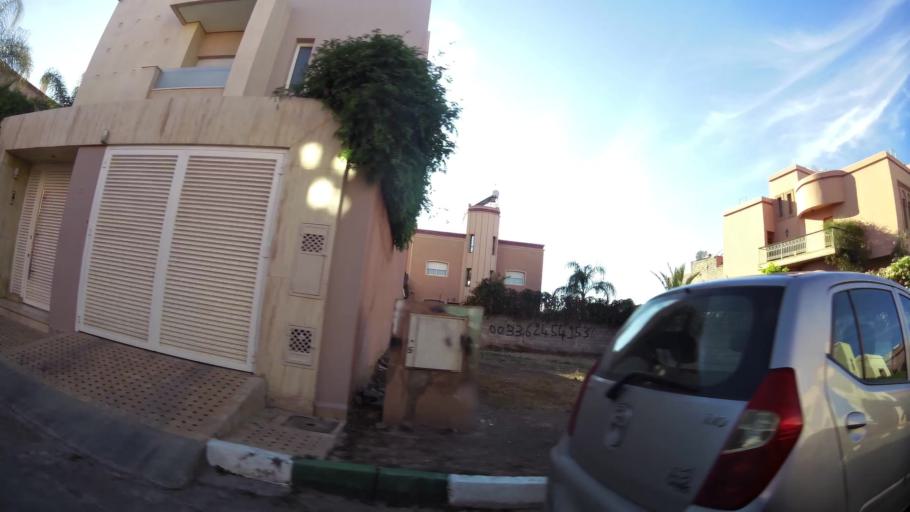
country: MA
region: Marrakech-Tensift-Al Haouz
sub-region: Marrakech
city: Marrakesh
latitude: 31.6624
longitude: -8.0611
